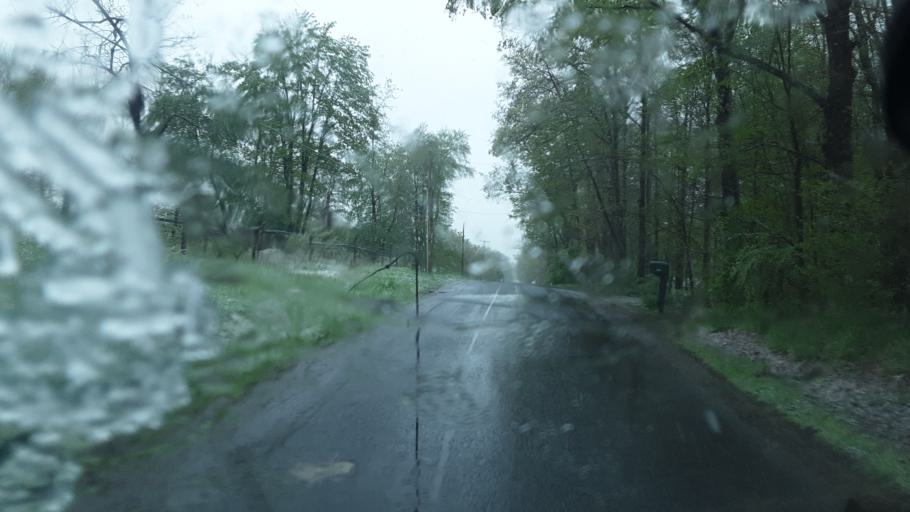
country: US
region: Ohio
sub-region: Portage County
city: Garrettsville
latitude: 41.3048
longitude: -81.0387
